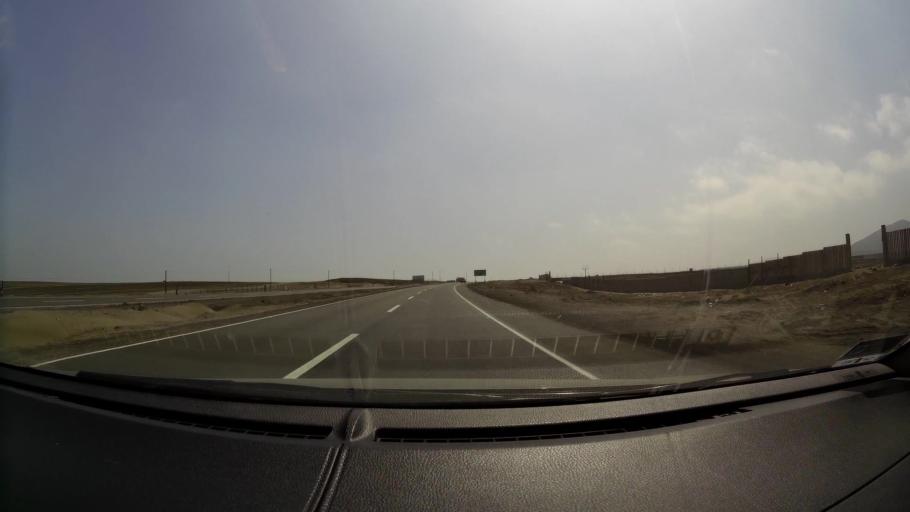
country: PE
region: Lima
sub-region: Provincia de Huaral
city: Chancay
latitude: -11.3969
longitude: -77.4212
